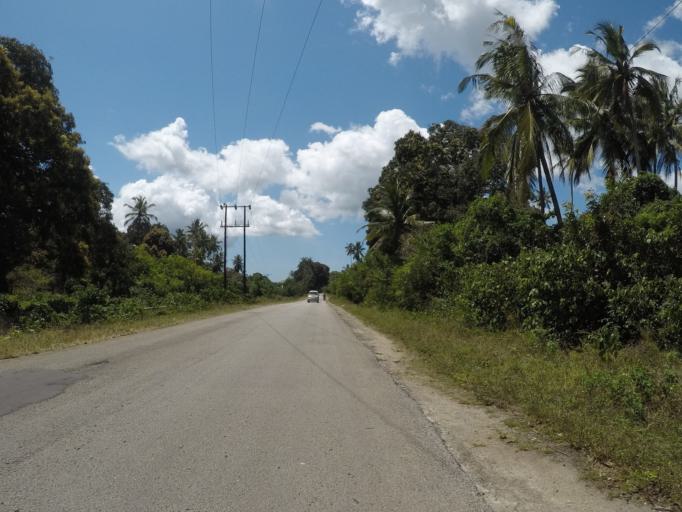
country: TZ
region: Zanzibar Central/South
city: Nganane
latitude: -6.2979
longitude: 39.4351
